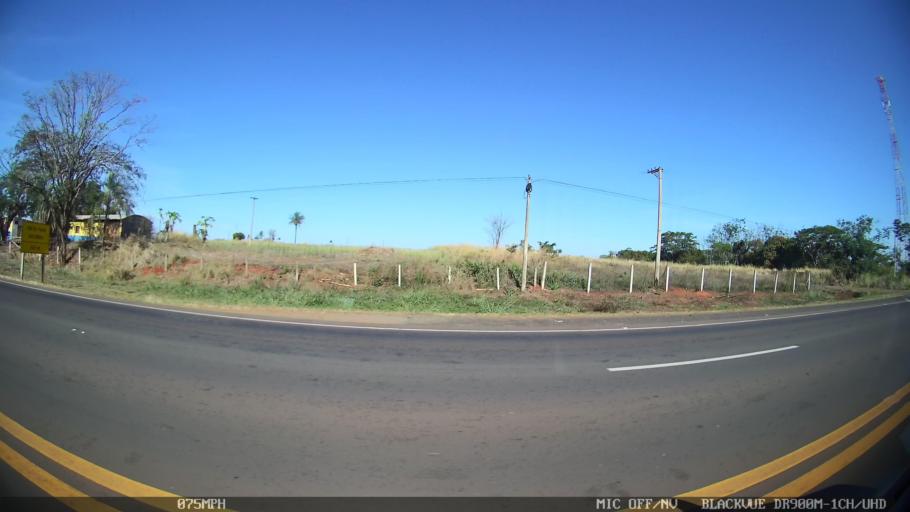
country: BR
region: Sao Paulo
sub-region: Olimpia
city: Olimpia
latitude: -20.6837
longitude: -48.9022
